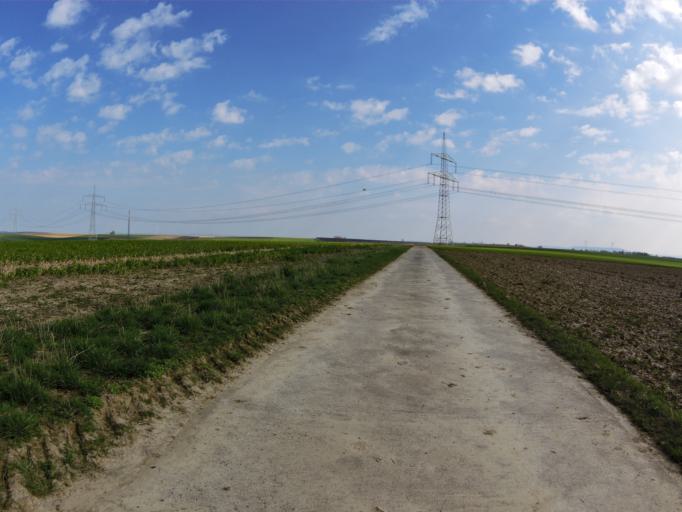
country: DE
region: Bavaria
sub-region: Regierungsbezirk Unterfranken
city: Rottendorf
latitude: 49.8020
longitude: 10.0638
